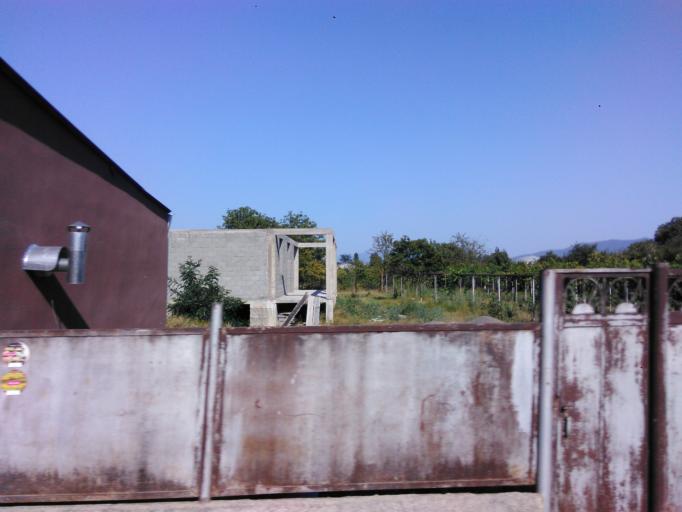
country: GE
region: Shida Kartli
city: Kaspi
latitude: 41.9378
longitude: 44.5786
